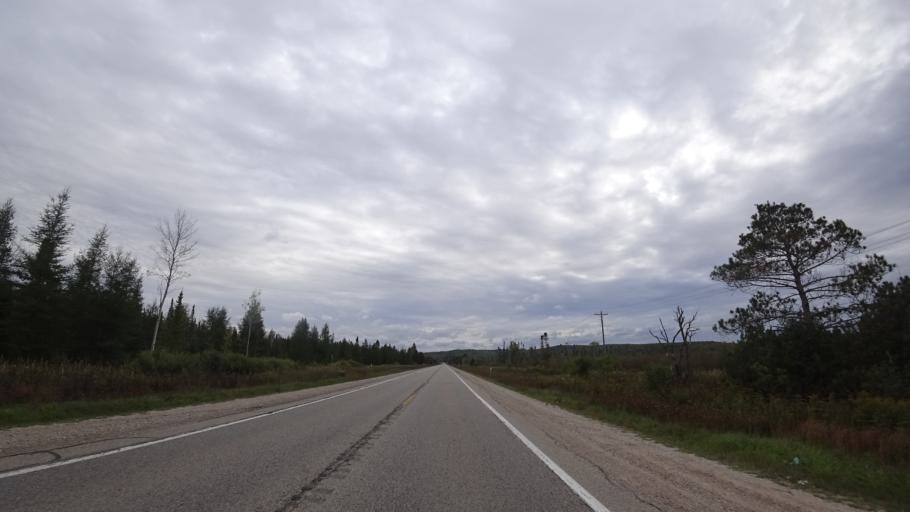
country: US
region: Michigan
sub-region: Charlevoix County
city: Boyne City
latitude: 45.2286
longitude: -84.9185
